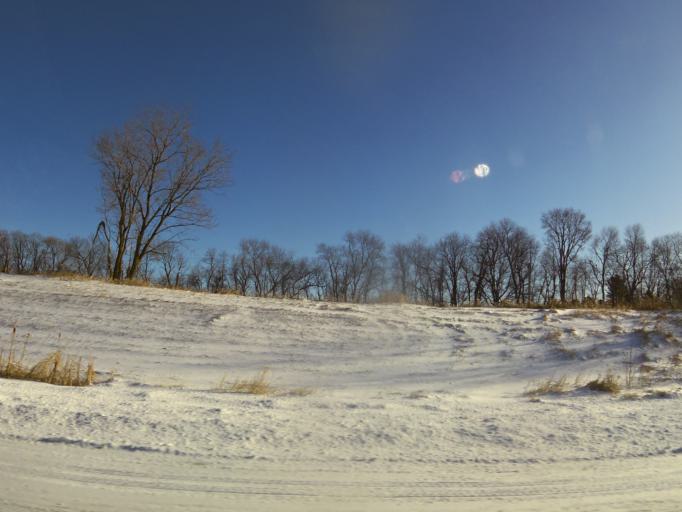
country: US
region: Minnesota
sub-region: Rice County
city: Faribault
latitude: 44.3718
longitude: -93.2932
